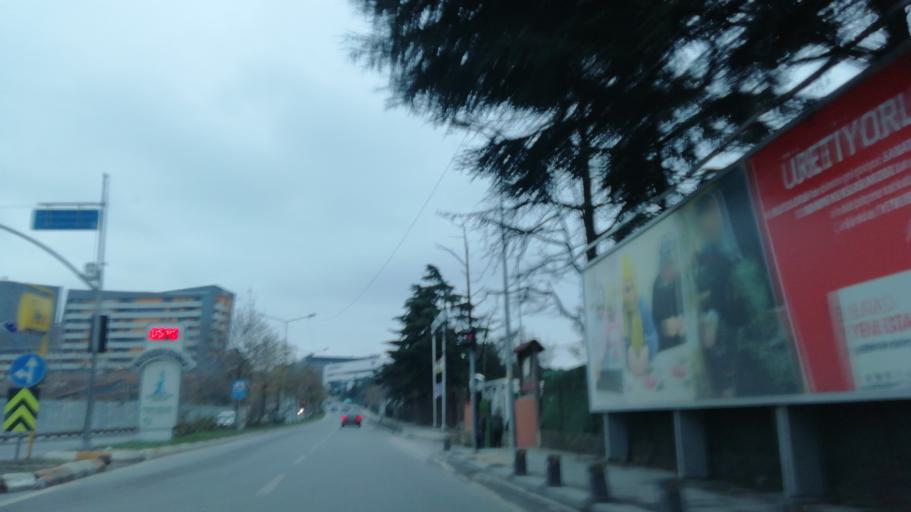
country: TR
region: Istanbul
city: Sultanbeyli
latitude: 40.9727
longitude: 29.2476
